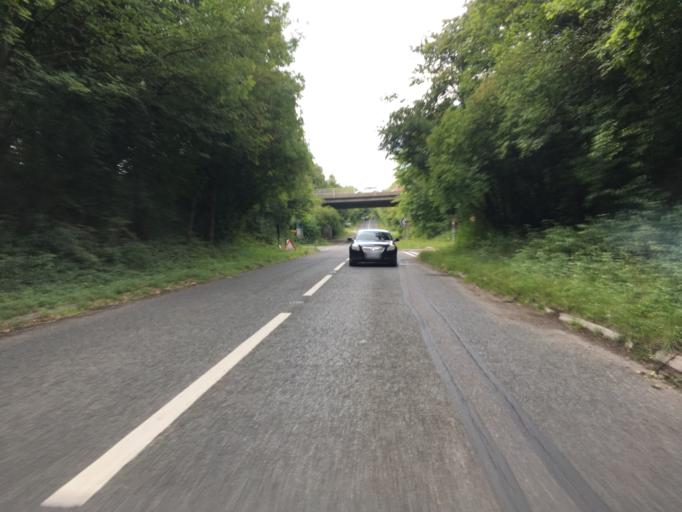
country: GB
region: England
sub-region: Hampshire
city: Overton
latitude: 51.1892
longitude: -1.2561
